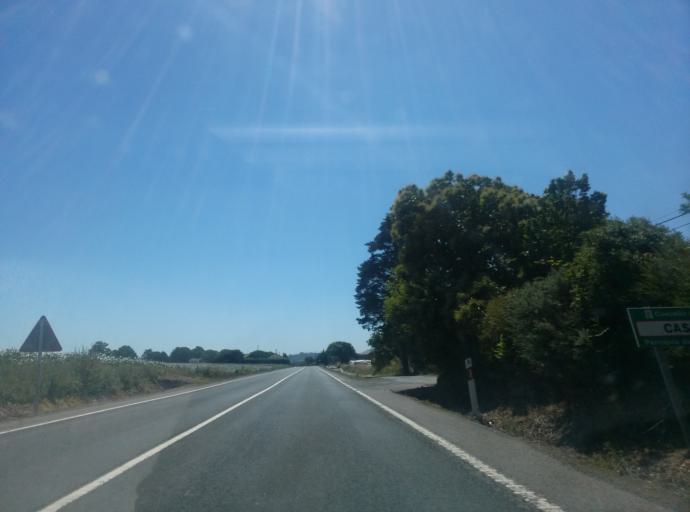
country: ES
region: Galicia
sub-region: Provincia de Lugo
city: Pol
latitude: 43.1890
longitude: -7.3425
